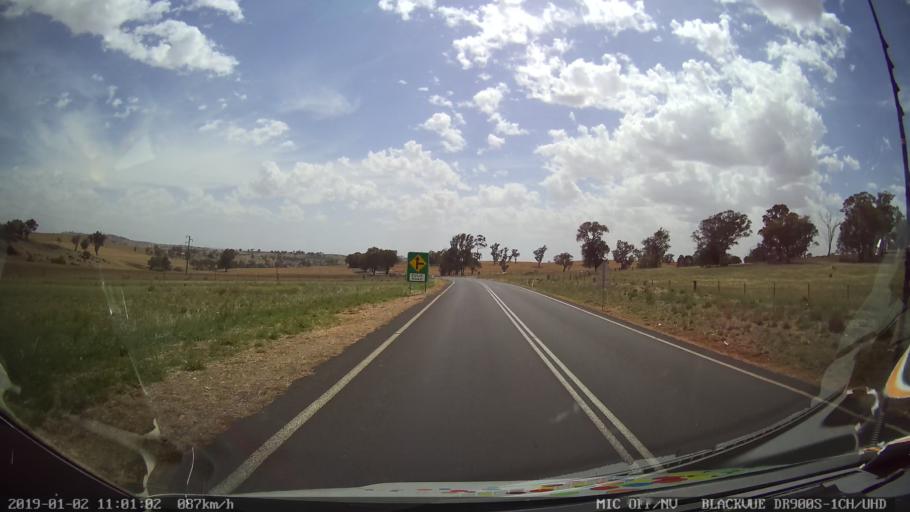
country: AU
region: New South Wales
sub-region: Young
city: Young
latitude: -34.6019
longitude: 148.3161
